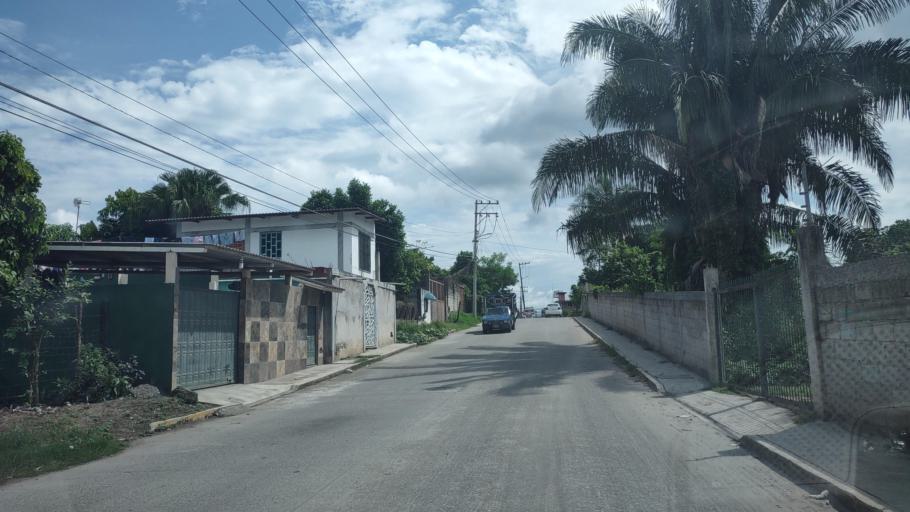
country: MX
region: Veracruz
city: Martinez de la Torre
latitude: 20.0703
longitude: -97.0741
